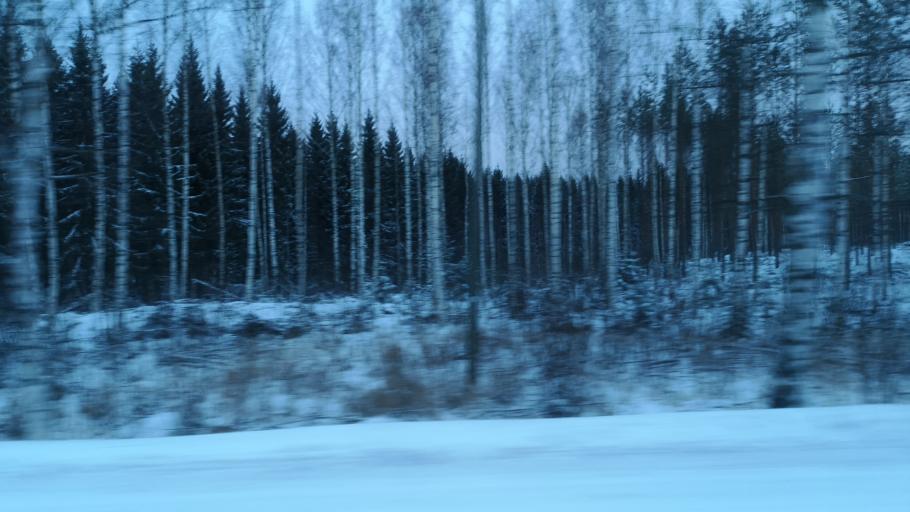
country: FI
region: Southern Savonia
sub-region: Savonlinna
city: Enonkoski
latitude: 62.0998
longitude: 28.6568
